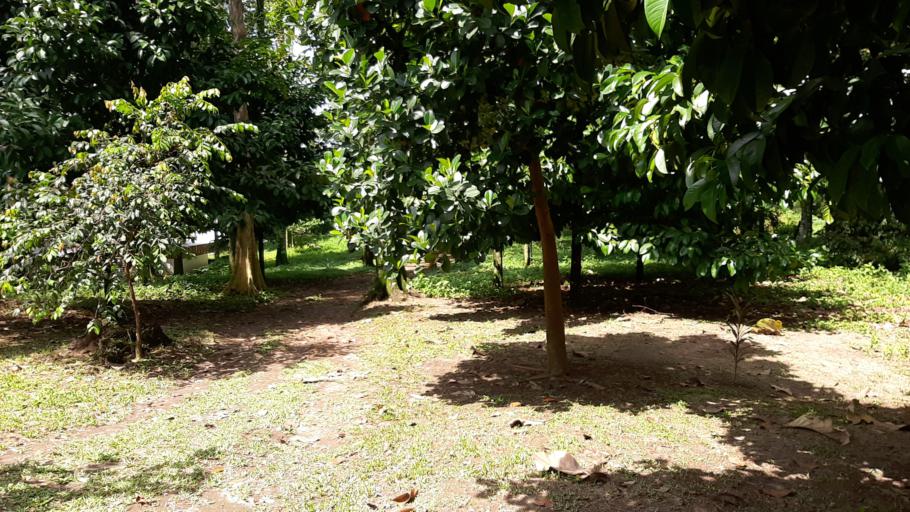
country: GT
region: Retalhuleu
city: San Felipe
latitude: 14.6102
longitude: -91.5781
